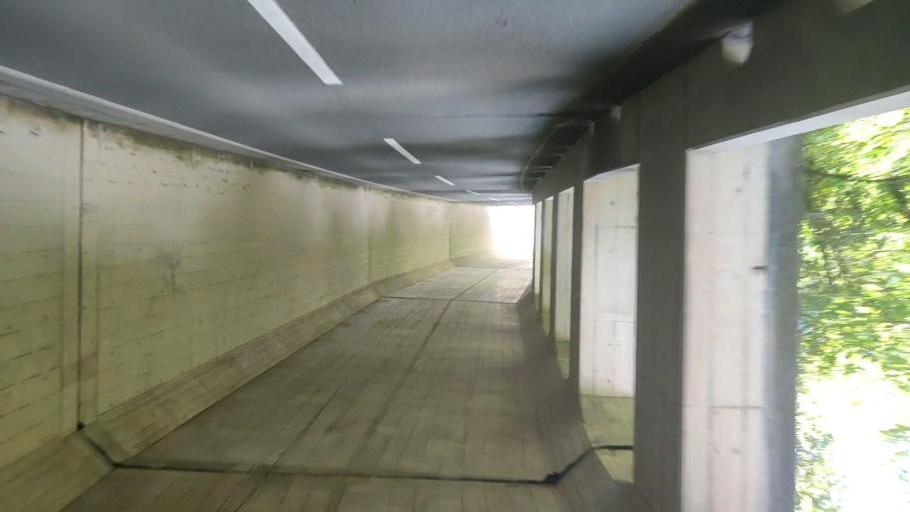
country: JP
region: Fukui
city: Ono
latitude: 35.8999
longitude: 136.5268
